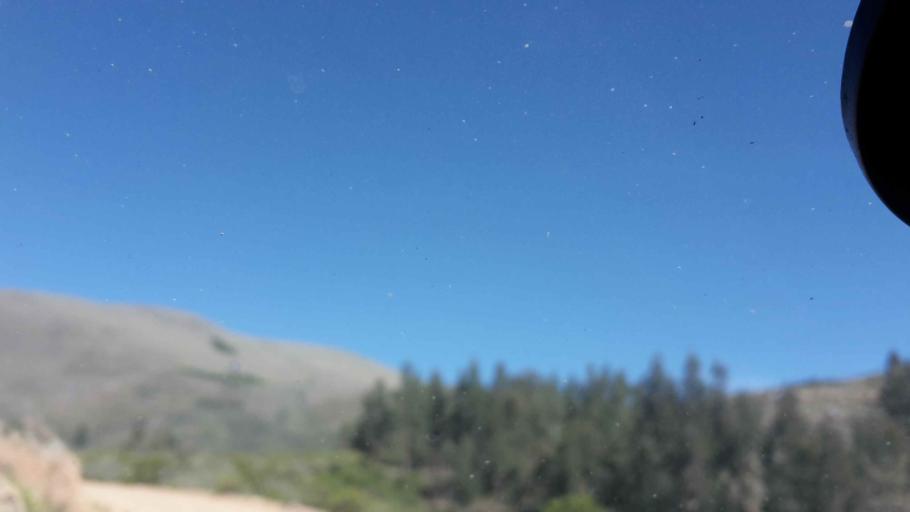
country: BO
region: Cochabamba
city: Arani
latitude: -17.6611
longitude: -65.7354
